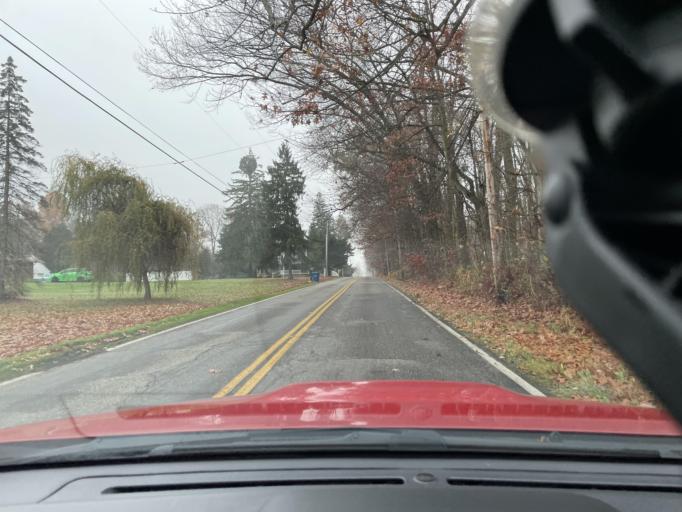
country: US
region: Ohio
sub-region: Trumbull County
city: Mineral Ridge
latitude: 41.1476
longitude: -80.7535
